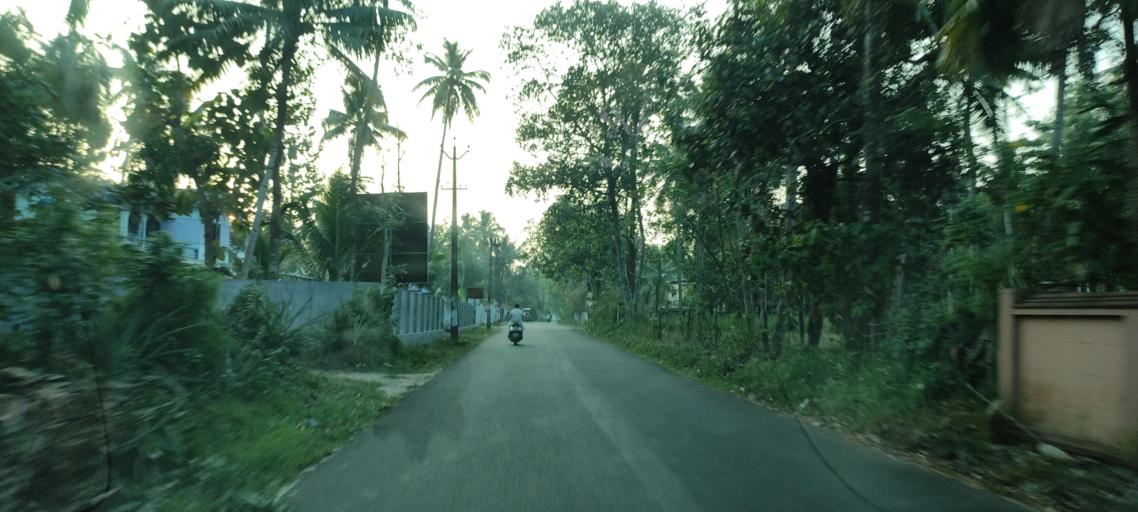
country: IN
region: Kerala
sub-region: Alappuzha
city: Kattanam
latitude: 9.1350
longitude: 76.5399
